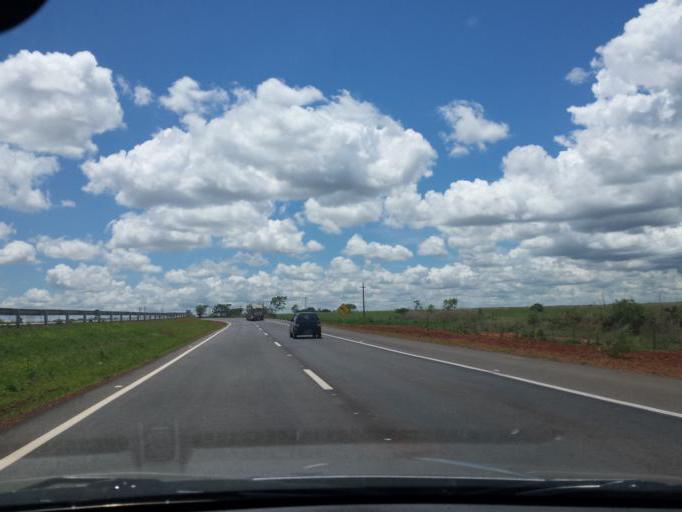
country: BR
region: Goias
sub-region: Cristalina
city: Cristalina
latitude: -16.7033
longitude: -47.6903
